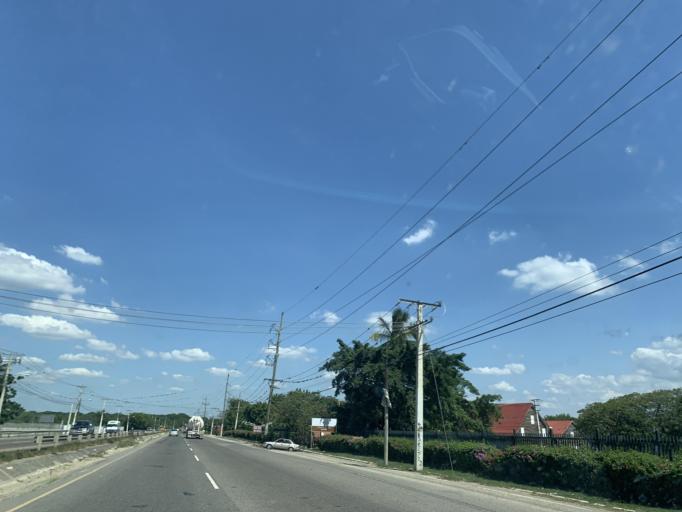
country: DO
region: Santiago
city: Villa Gonzalez
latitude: 19.5284
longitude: -70.7749
